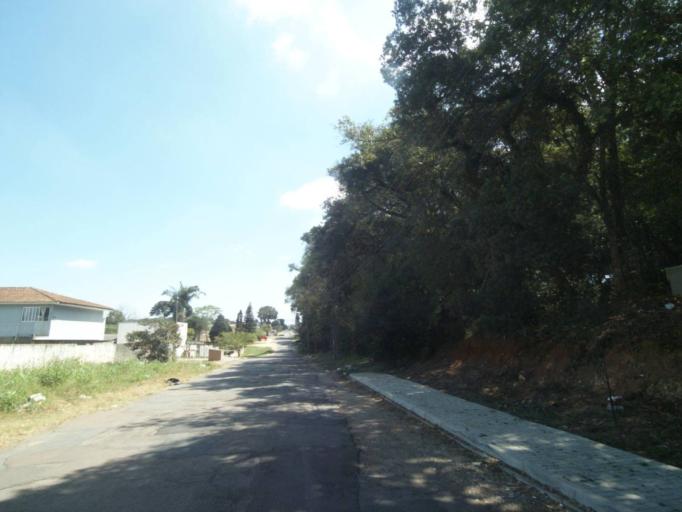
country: BR
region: Parana
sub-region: Sao Jose Dos Pinhais
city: Sao Jose dos Pinhais
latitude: -25.5180
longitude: -49.2458
